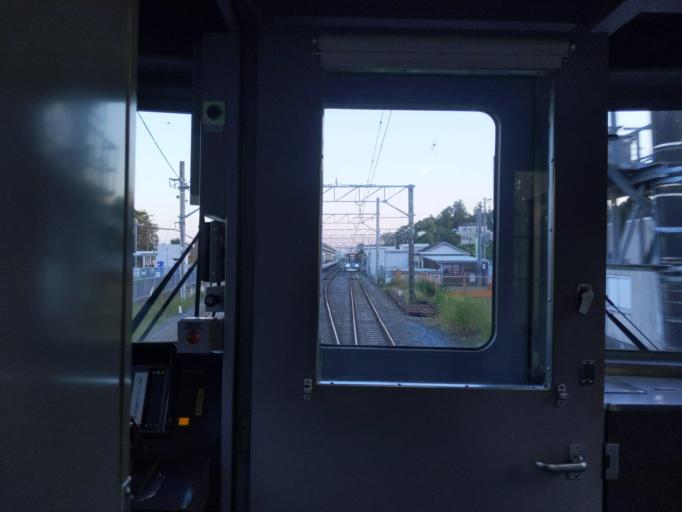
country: JP
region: Chiba
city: Noda
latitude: 35.9600
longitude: 139.8594
